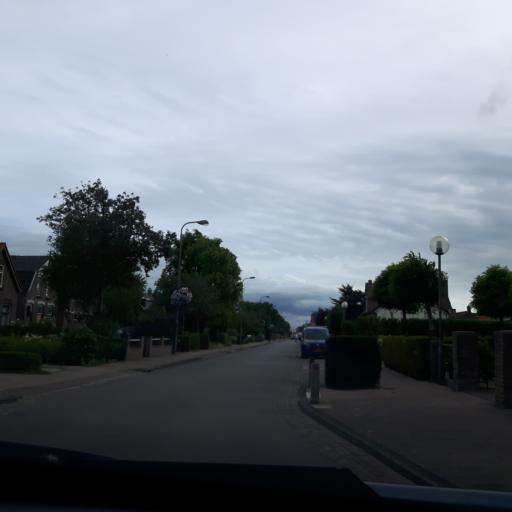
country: NL
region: Zeeland
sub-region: Gemeente Noord-Beveland
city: Kamperland
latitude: 51.5701
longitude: 3.7026
